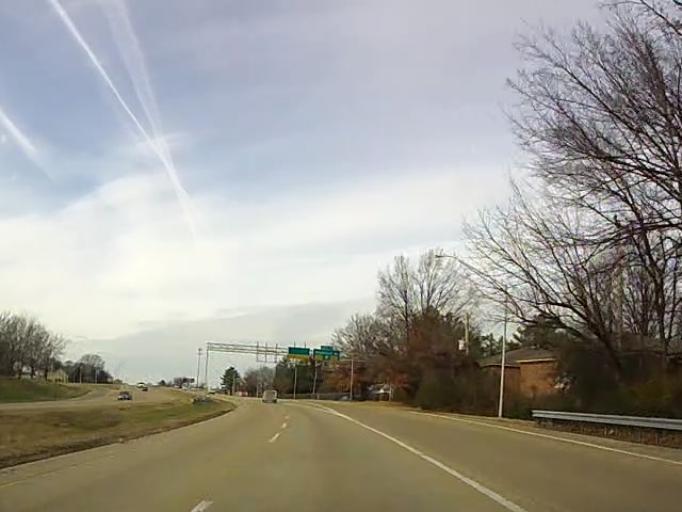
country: US
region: Tennessee
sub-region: Shelby County
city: Bartlett
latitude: 35.1482
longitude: -89.9414
